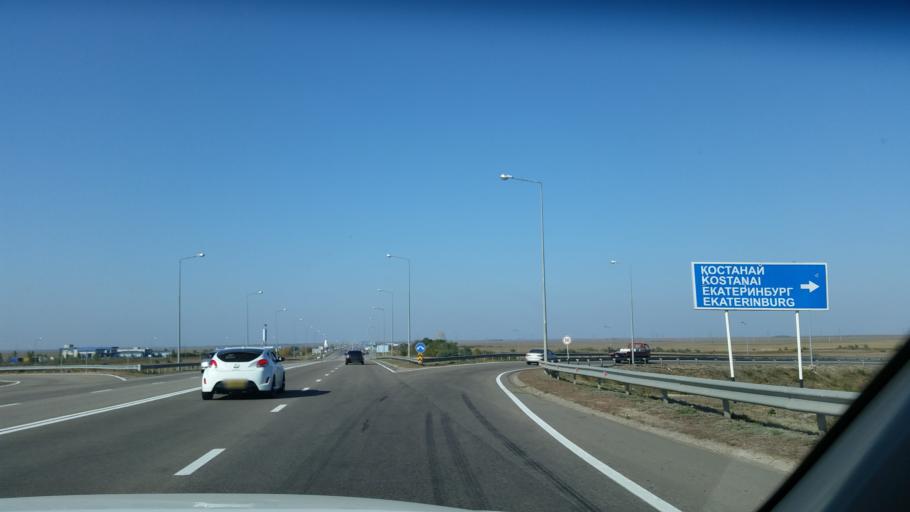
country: KZ
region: Astana Qalasy
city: Astana
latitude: 51.2562
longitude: 71.3739
